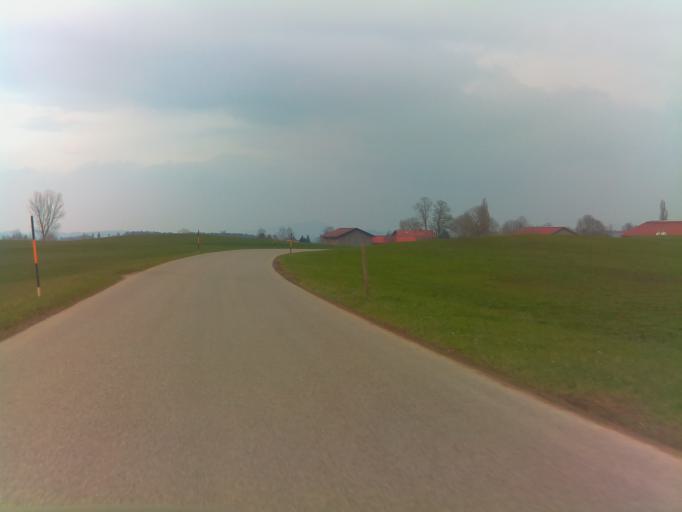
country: DE
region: Bavaria
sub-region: Upper Bavaria
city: Ingenried
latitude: 47.8191
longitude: 10.7713
